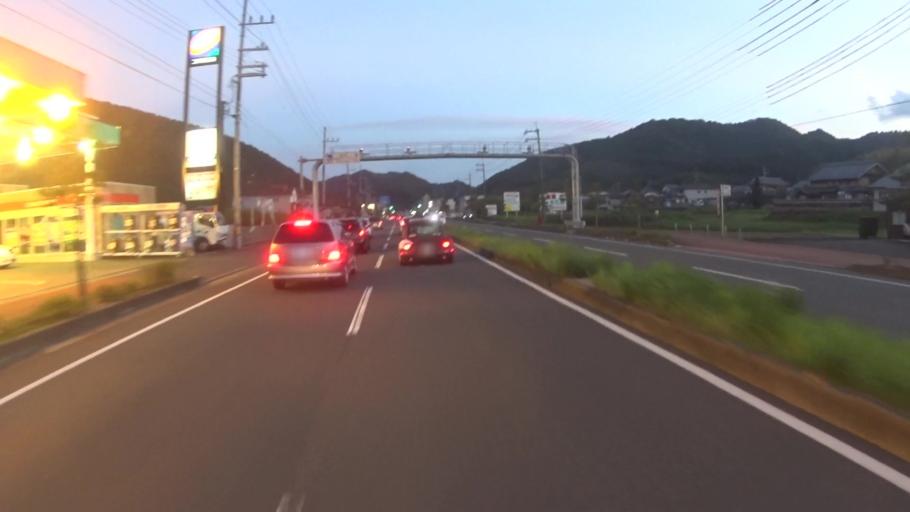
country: JP
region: Kyoto
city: Kameoka
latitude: 35.1590
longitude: 135.4260
